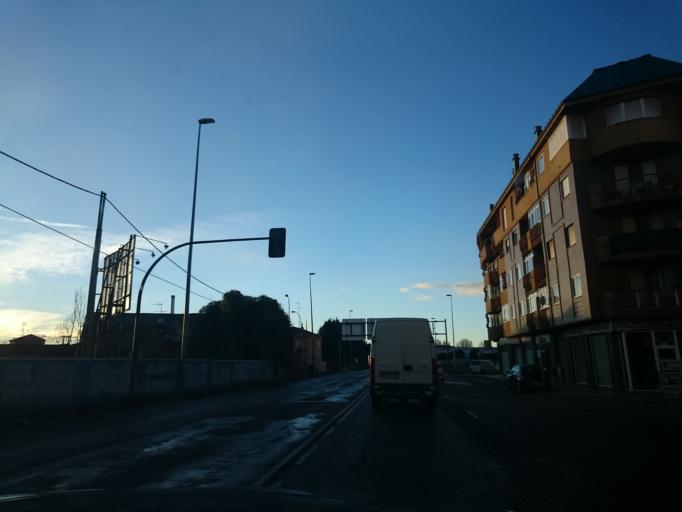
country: ES
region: Castille and Leon
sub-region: Provincia de Leon
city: Leon
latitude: 42.5825
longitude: -5.5840
